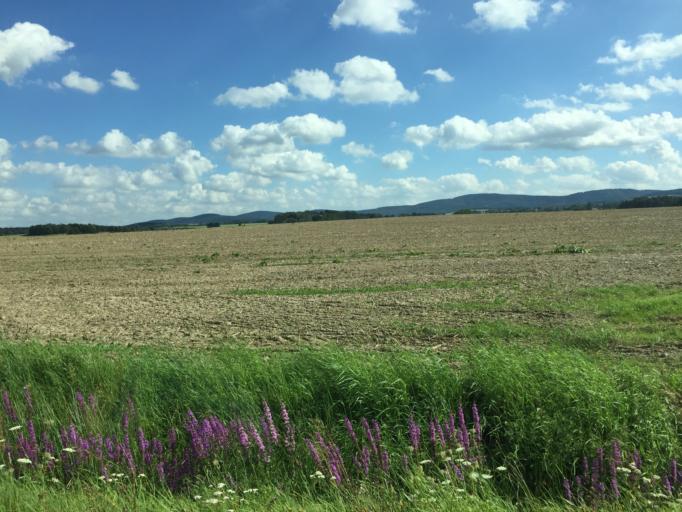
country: DE
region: Saxony
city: Kubschutz
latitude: 51.1850
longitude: 14.5081
